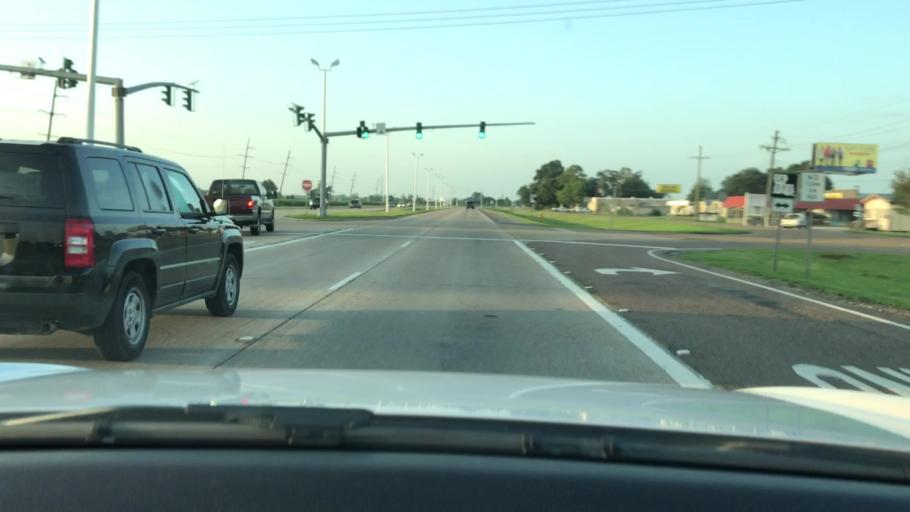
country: US
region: Louisiana
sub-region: West Baton Rouge Parish
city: Addis
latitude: 30.3560
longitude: -91.2597
